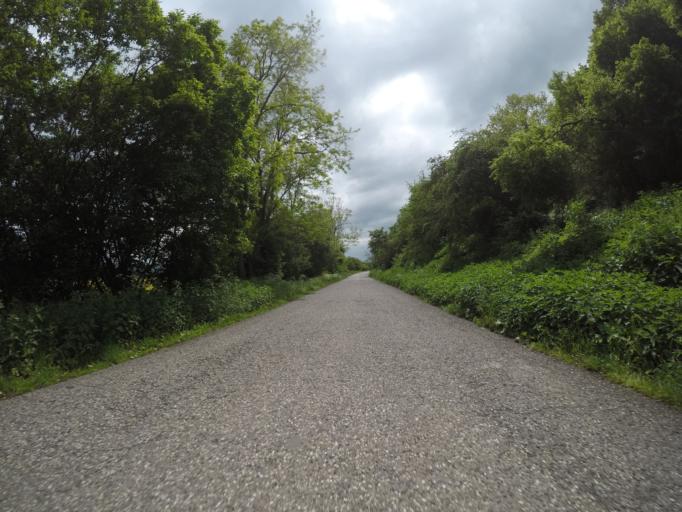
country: SK
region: Banskobystricky
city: Dudince
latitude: 48.1031
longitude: 18.8699
